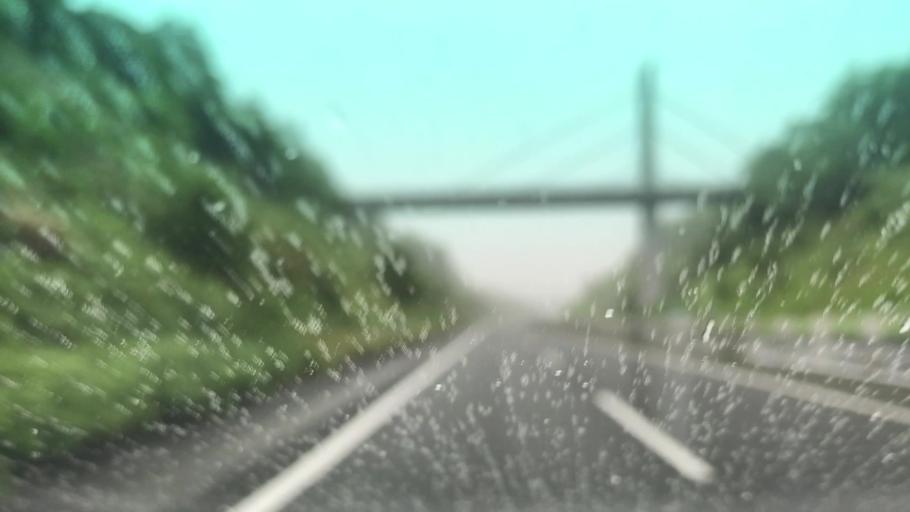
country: JP
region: Hokkaido
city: Tomakomai
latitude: 42.6258
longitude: 141.4822
